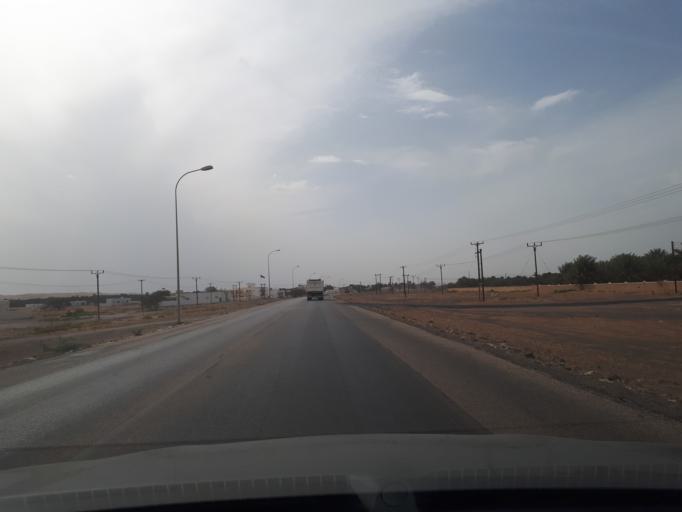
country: OM
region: Ash Sharqiyah
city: Badiyah
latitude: 22.4947
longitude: 58.7569
